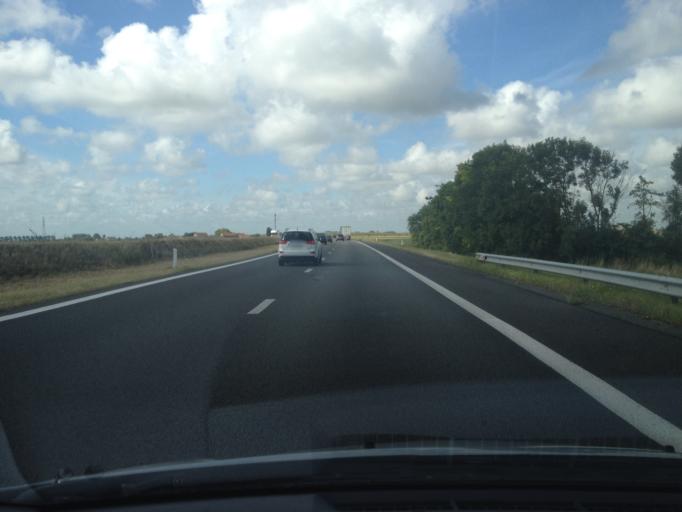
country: BE
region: Flanders
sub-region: Provincie West-Vlaanderen
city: Nieuwpoort
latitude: 51.1014
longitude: 2.7395
